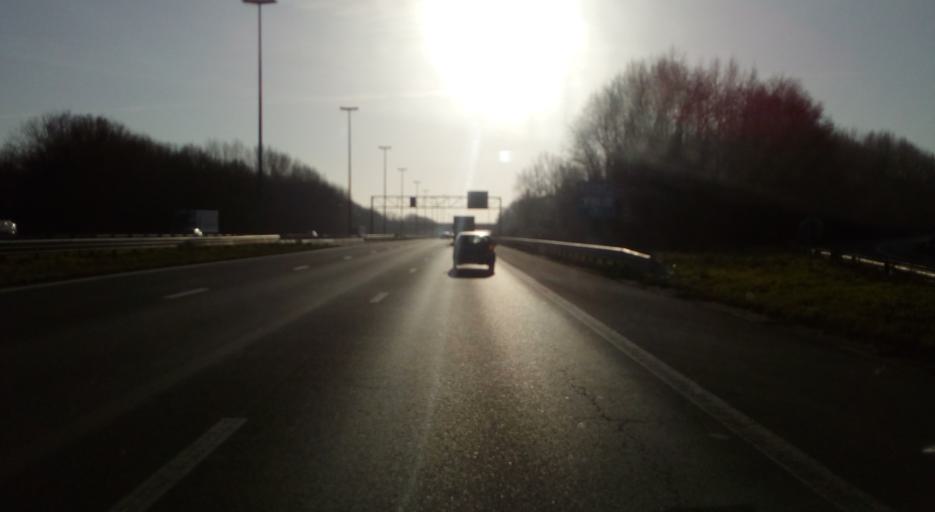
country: BE
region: Wallonia
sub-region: Province du Brabant Wallon
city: Braine-le-Chateau
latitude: 50.6655
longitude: 4.3107
